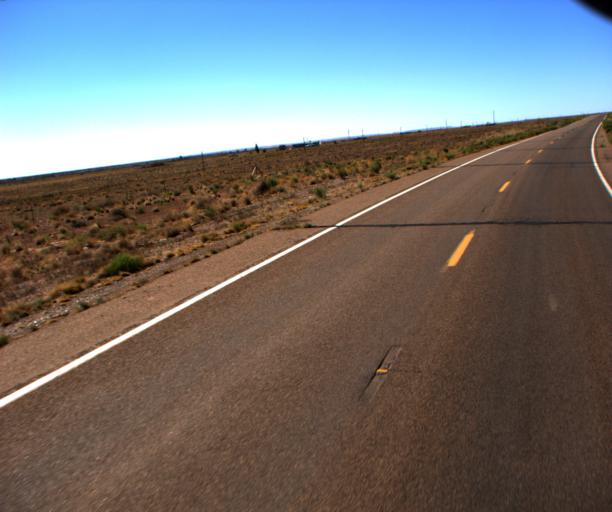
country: US
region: Arizona
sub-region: Coconino County
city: LeChee
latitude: 35.2885
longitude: -110.9847
